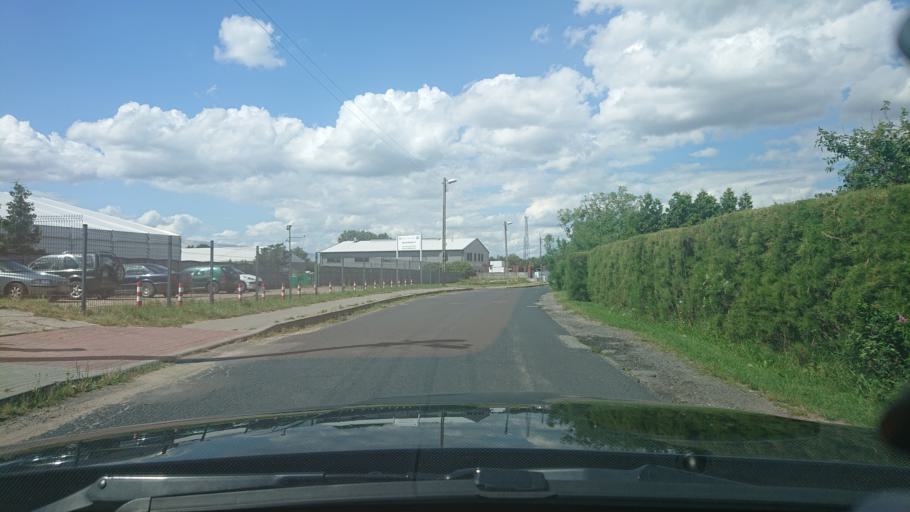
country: PL
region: Greater Poland Voivodeship
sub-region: Powiat gnieznienski
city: Gniezno
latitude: 52.5367
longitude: 17.6341
